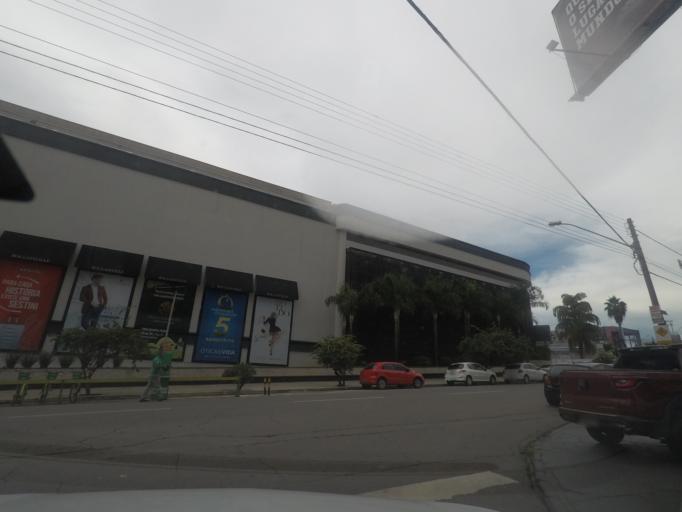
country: BR
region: Goias
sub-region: Goiania
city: Goiania
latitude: -16.6955
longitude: -49.2659
